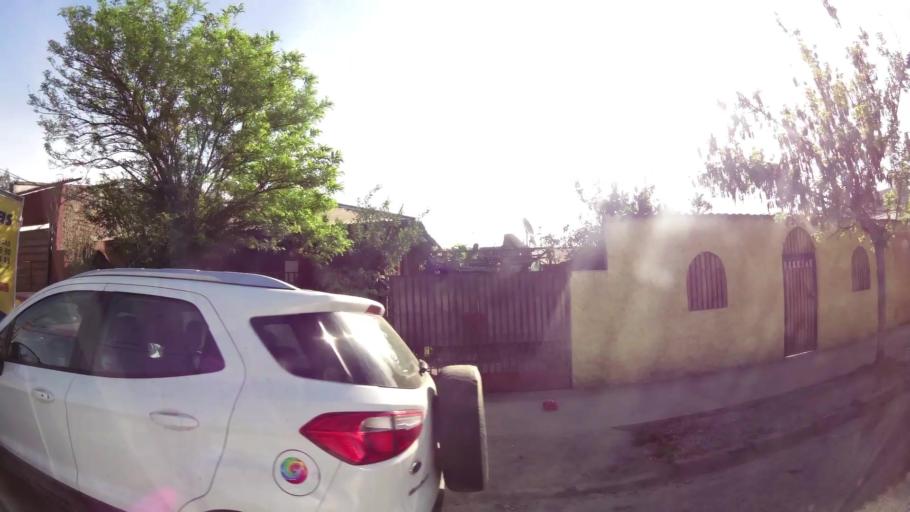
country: CL
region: Santiago Metropolitan
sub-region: Provincia de Santiago
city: Santiago
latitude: -33.5137
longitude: -70.6311
